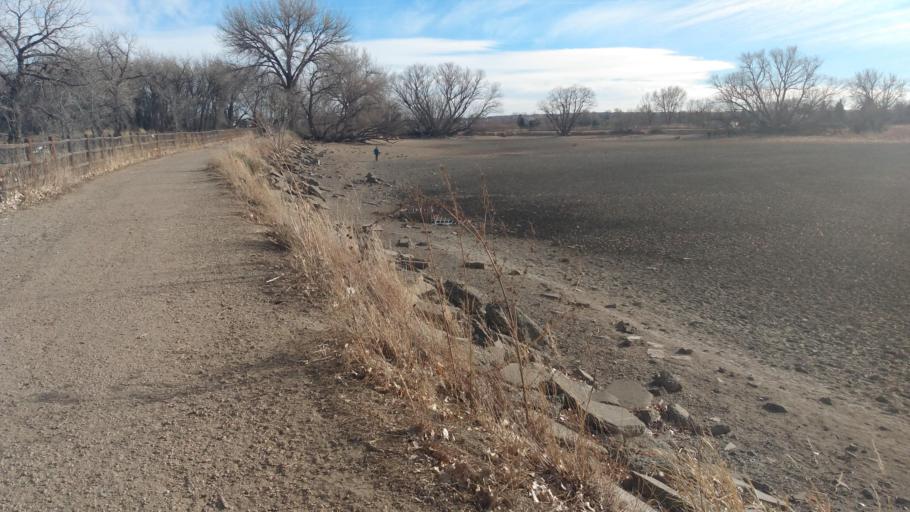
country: US
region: Colorado
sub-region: Boulder County
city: Gunbarrel
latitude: 40.0622
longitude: -105.2005
